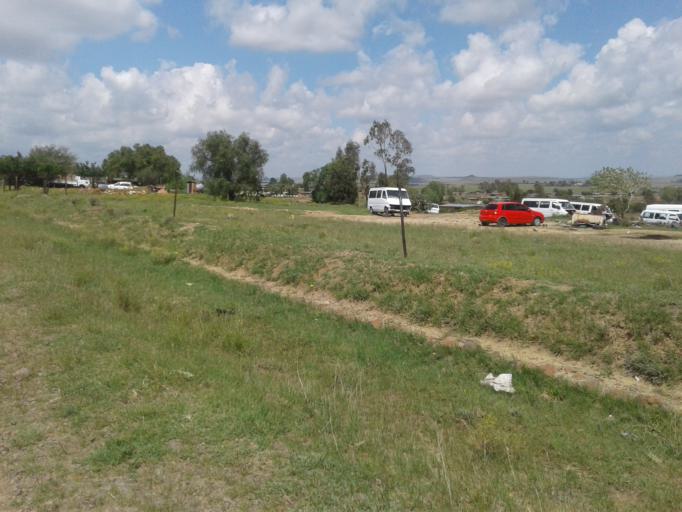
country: LS
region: Mafeteng
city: Mafeteng
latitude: -29.7477
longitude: 27.1136
